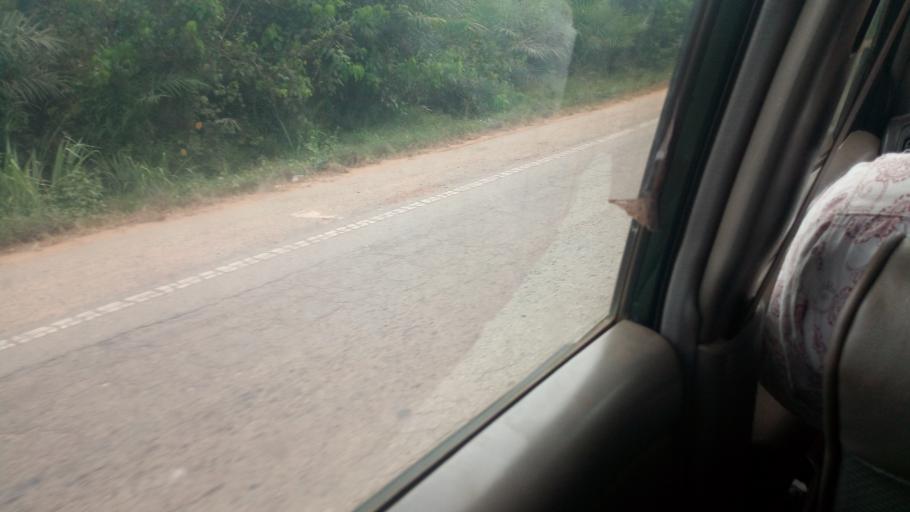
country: GH
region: Western
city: Takoradi
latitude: 4.8975
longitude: -1.9624
